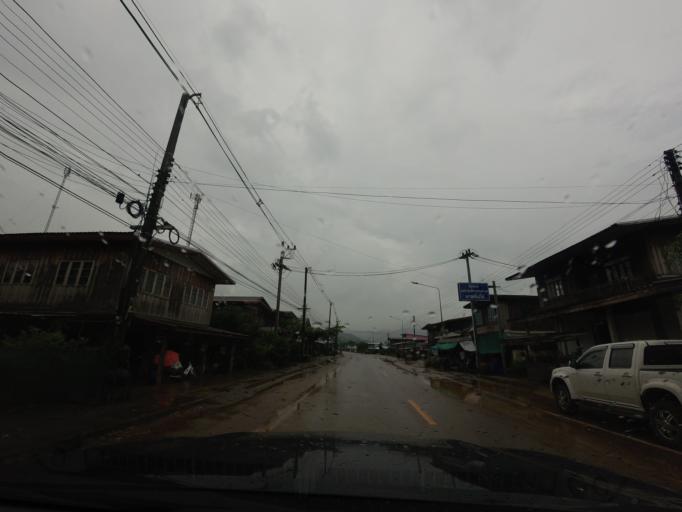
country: TH
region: Loei
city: Pak Chom
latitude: 18.1997
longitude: 102.0599
